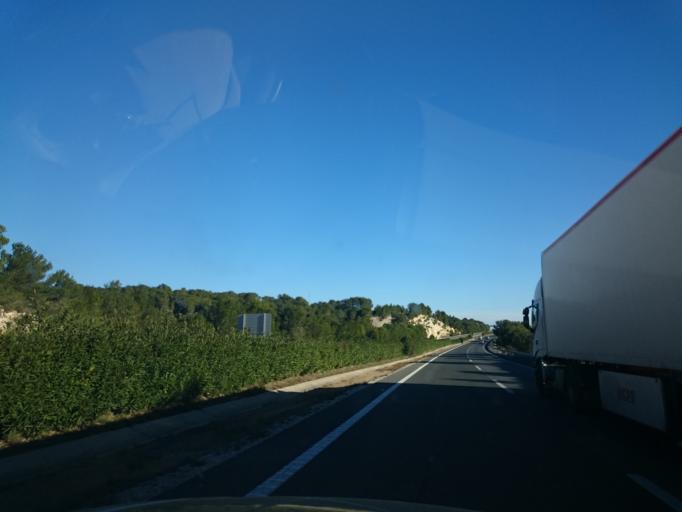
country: ES
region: Catalonia
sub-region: Provincia de Tarragona
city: El Perello
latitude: 40.8457
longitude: 0.7495
